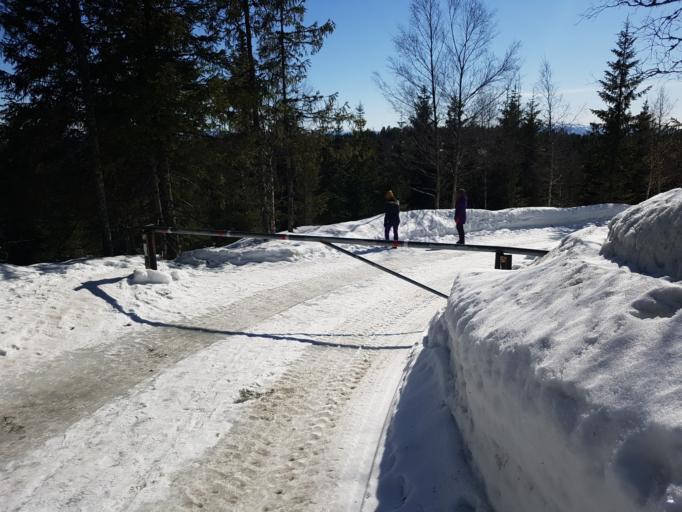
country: NO
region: Sor-Trondelag
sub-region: Trondheim
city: Trondheim
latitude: 63.4150
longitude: 10.2775
